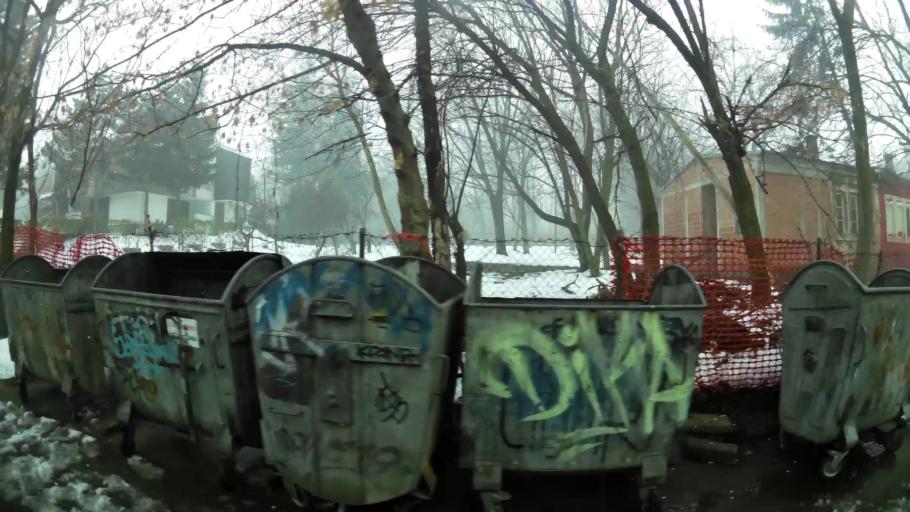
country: RS
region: Central Serbia
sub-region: Belgrade
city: Savski Venac
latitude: 44.7733
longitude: 20.4602
